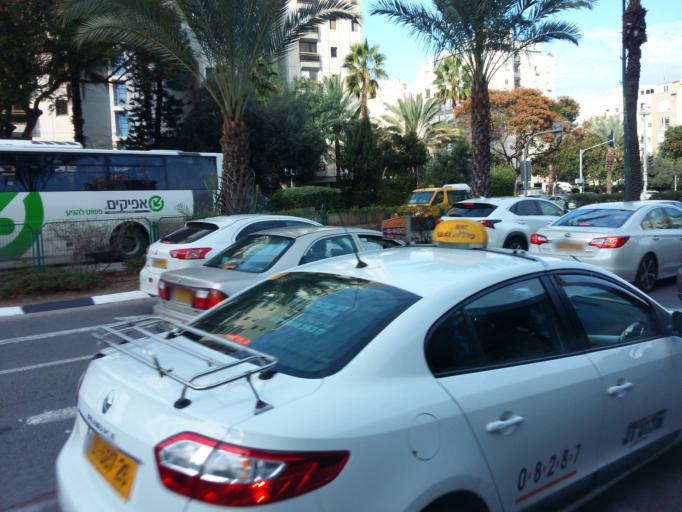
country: IL
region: Tel Aviv
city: Ramat Gan
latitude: 32.0888
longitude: 34.7954
